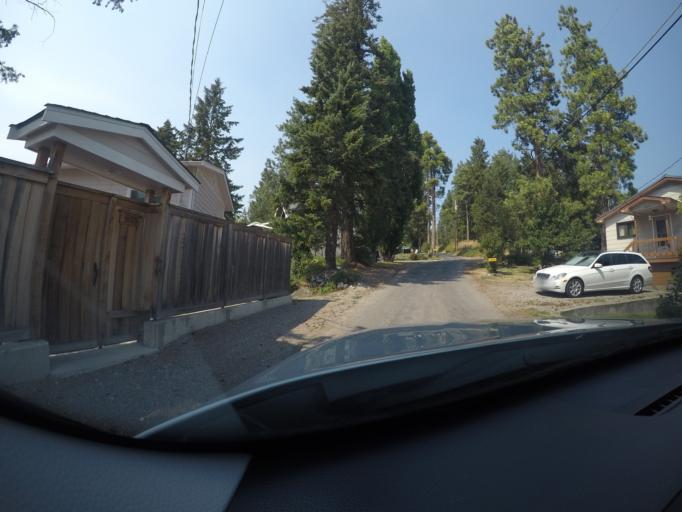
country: US
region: Montana
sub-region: Lake County
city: Polson
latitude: 47.7682
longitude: -114.1429
